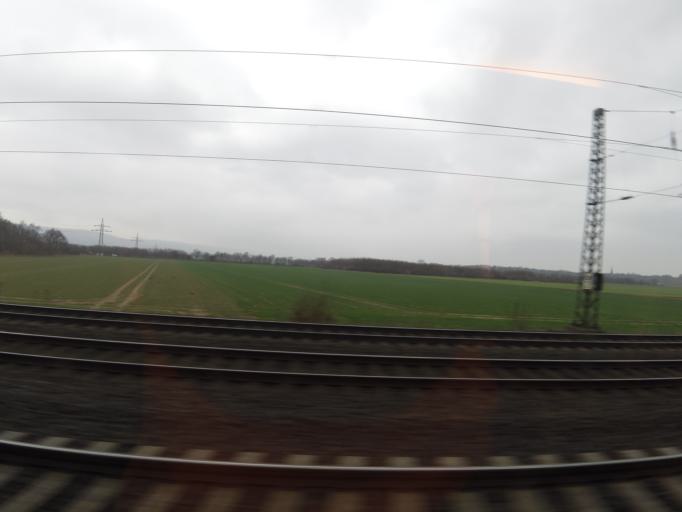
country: DE
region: North Rhine-Westphalia
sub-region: Regierungsbezirk Detmold
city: Minden
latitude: 52.2742
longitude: 8.9330
